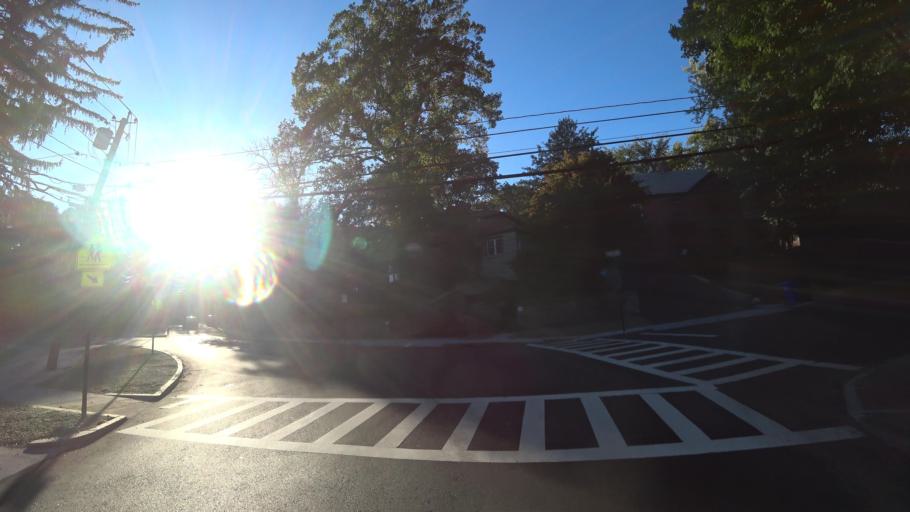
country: US
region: Massachusetts
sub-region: Norfolk County
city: Brookline
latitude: 42.3330
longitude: -71.1311
